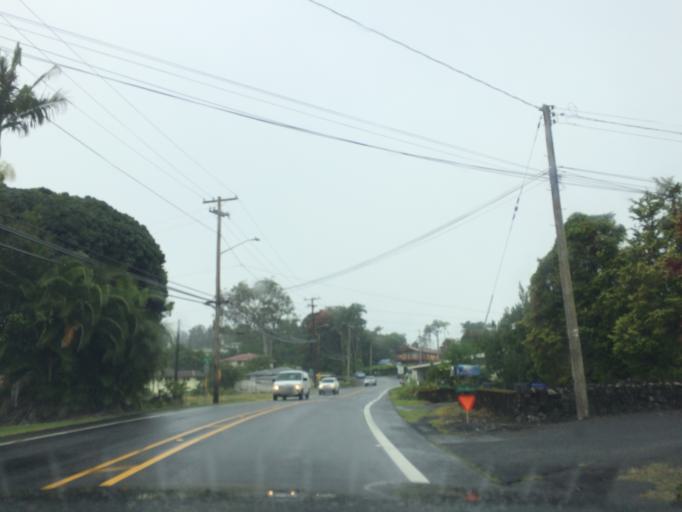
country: US
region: Hawaii
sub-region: Hawaii County
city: Hilo
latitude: 19.7032
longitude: -155.1120
